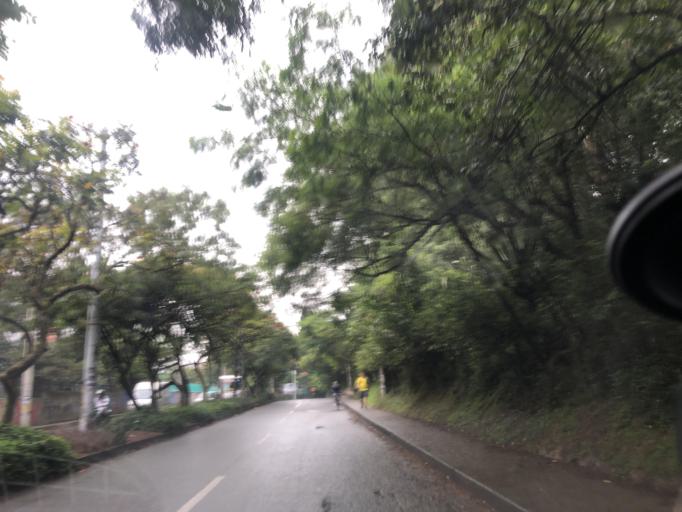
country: CO
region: Antioquia
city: Bello
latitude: 6.3251
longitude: -75.5611
